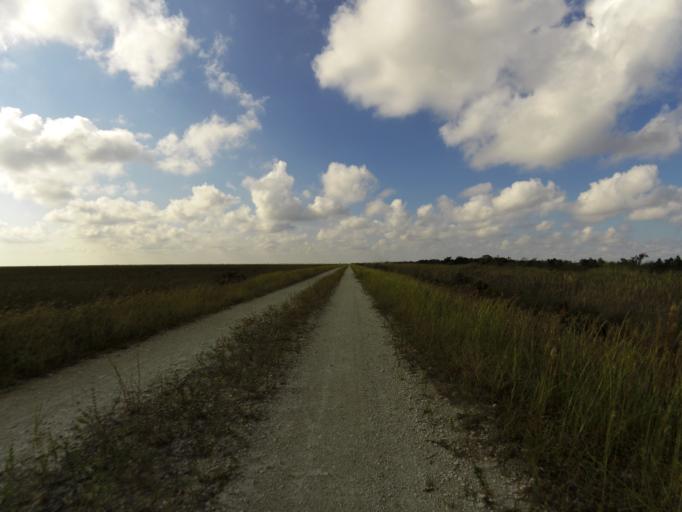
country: US
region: Florida
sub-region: Broward County
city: Weston
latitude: 26.0437
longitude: -80.4855
